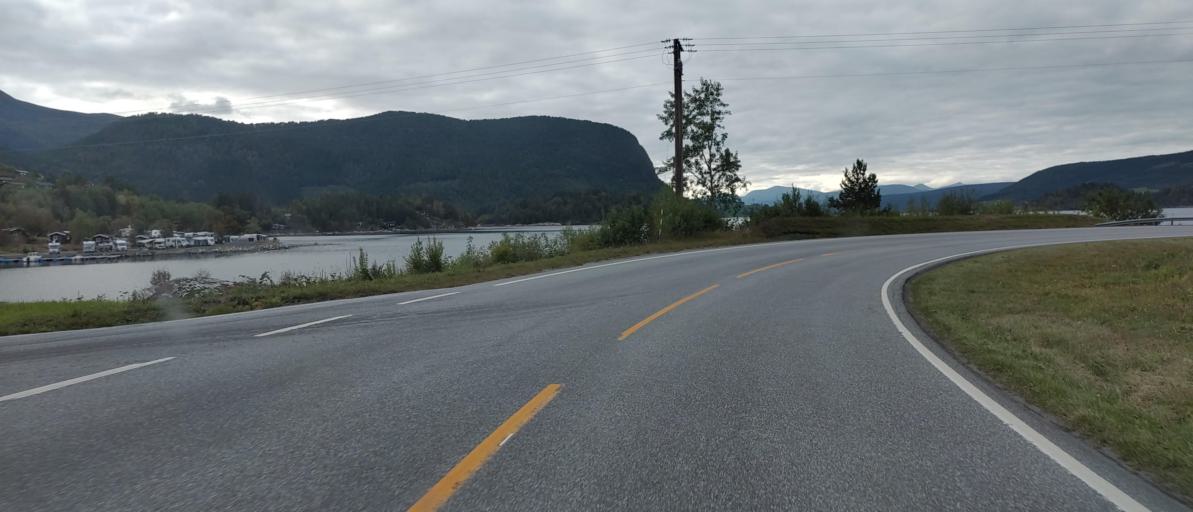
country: NO
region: More og Romsdal
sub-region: Rauma
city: Andalsnes
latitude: 62.5866
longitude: 7.5371
